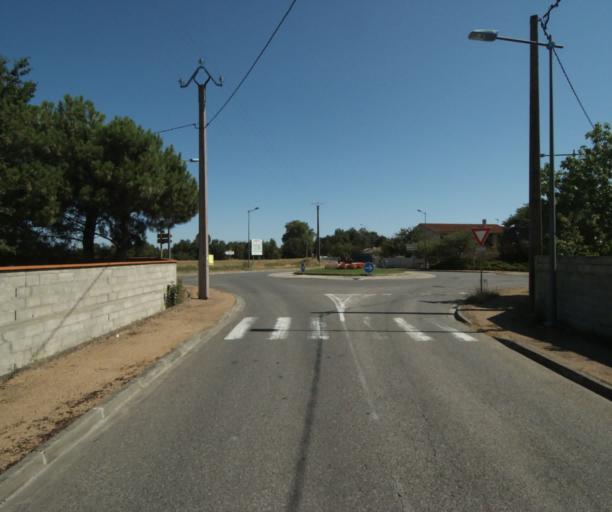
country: FR
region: Midi-Pyrenees
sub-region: Departement de la Haute-Garonne
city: Revel
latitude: 43.4645
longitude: 1.9887
